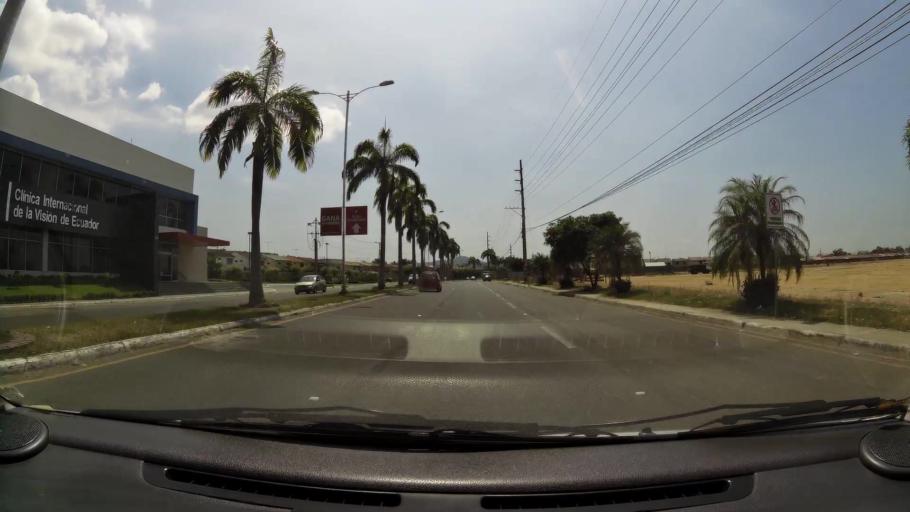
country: EC
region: Guayas
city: Eloy Alfaro
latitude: -2.0483
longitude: -79.8903
